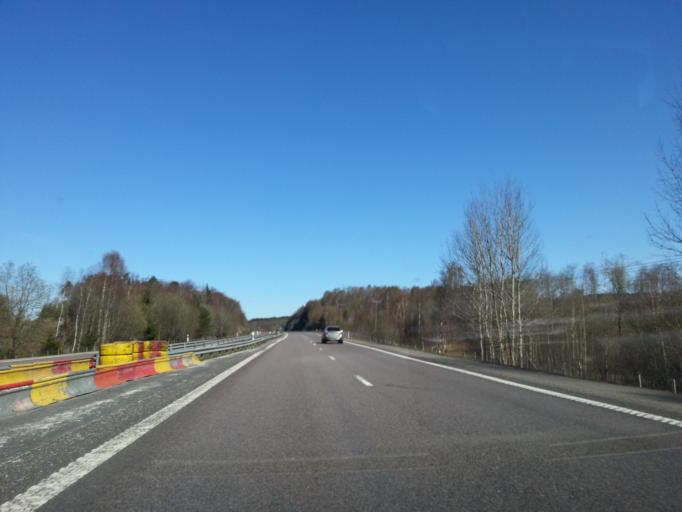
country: SE
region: Vaestra Goetaland
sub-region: Kungalvs Kommun
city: Kode
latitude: 57.9271
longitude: 11.8762
